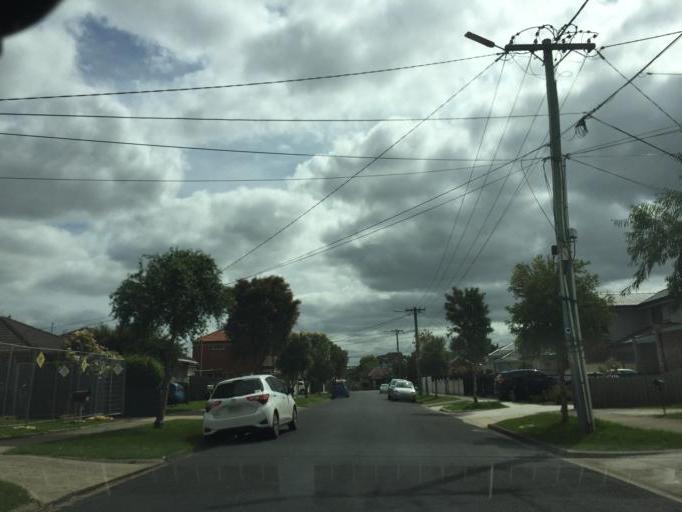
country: AU
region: Victoria
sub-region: Maribyrnong
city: Kingsville
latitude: -37.8140
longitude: 144.8669
